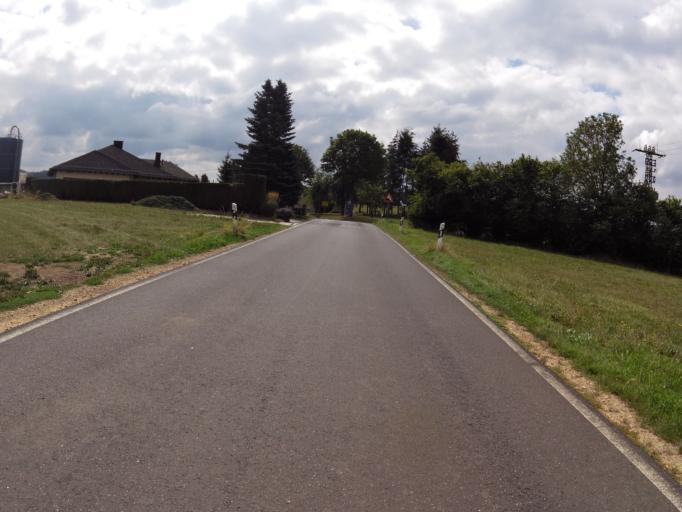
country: DE
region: Rheinland-Pfalz
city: Dohm-Lammersdorf
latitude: 50.2758
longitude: 6.6534
